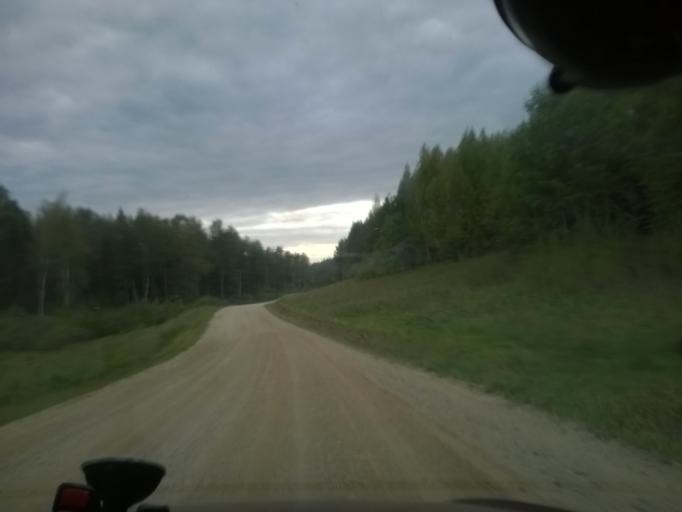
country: EE
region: Vorumaa
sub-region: Voru linn
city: Voru
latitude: 57.8135
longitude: 27.1549
